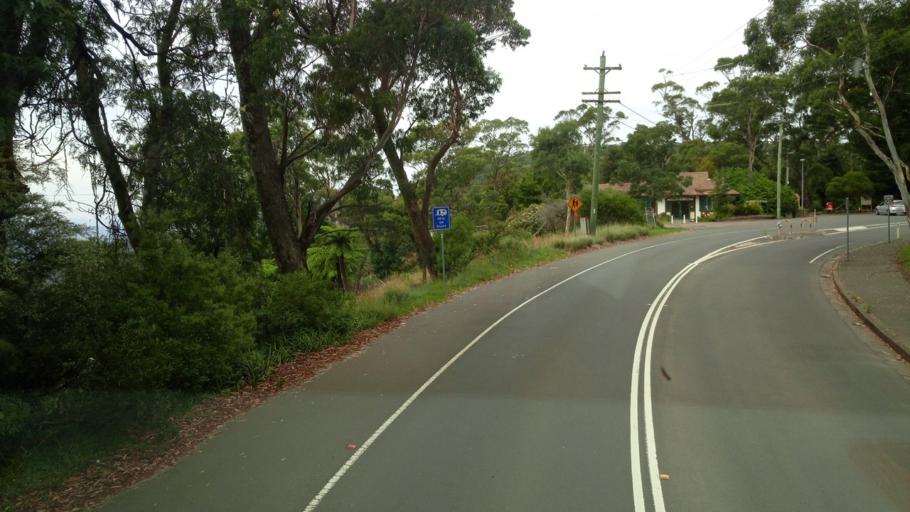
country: AU
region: New South Wales
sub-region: Blue Mountains Municipality
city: Katoomba
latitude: -33.7261
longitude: 150.3048
